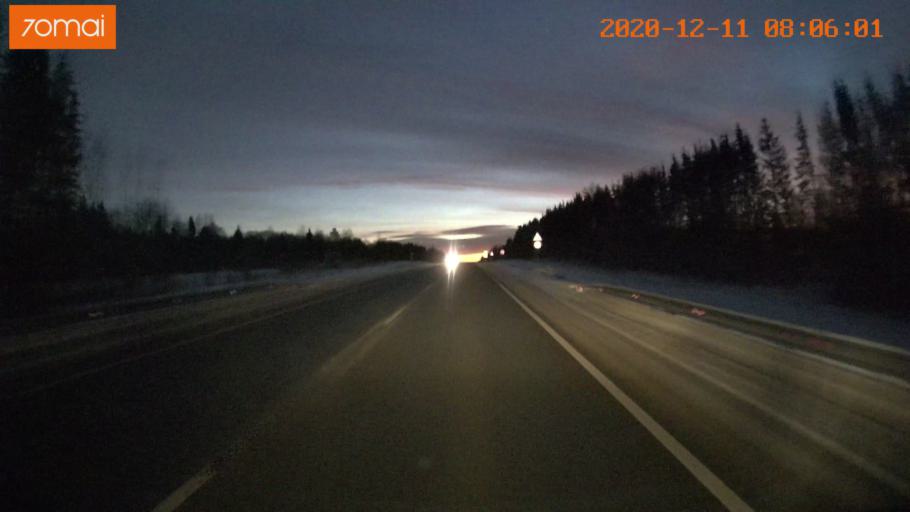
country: RU
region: Vologda
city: Chebsara
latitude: 59.1192
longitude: 39.0359
